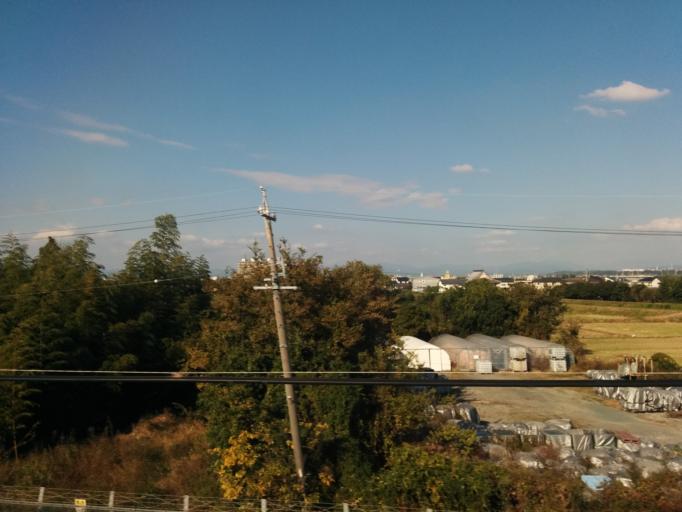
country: JP
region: Shizuoka
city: Iwata
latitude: 34.7028
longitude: 137.8247
